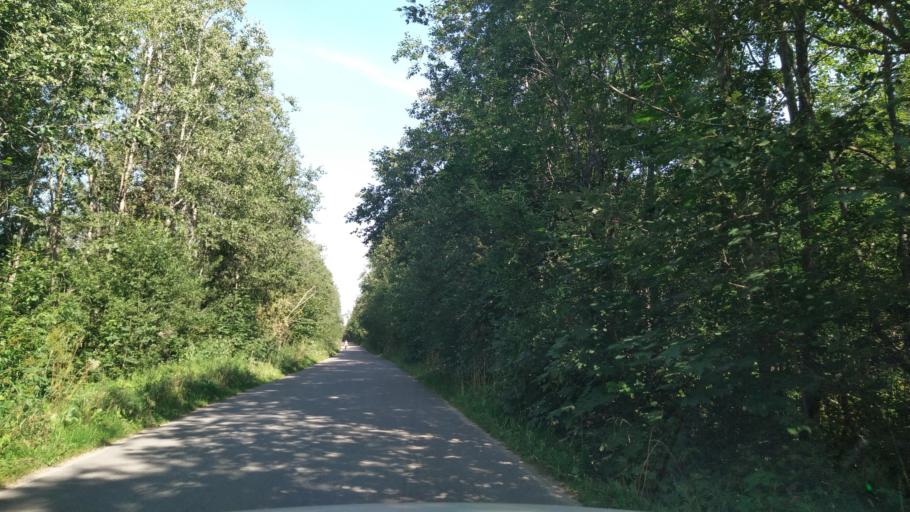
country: RU
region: Leningrad
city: Rozhdestveno
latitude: 59.2782
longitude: 30.0279
